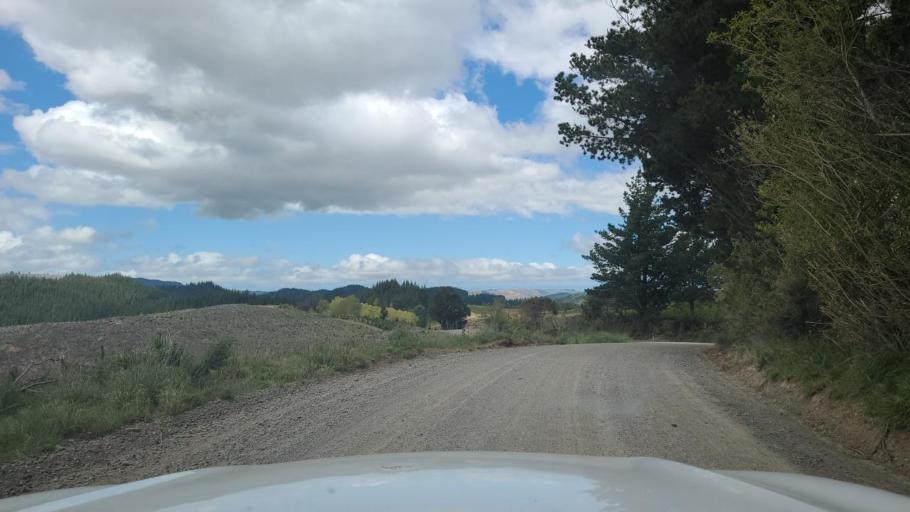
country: NZ
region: Hawke's Bay
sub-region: Napier City
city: Napier
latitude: -39.2483
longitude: 176.7264
